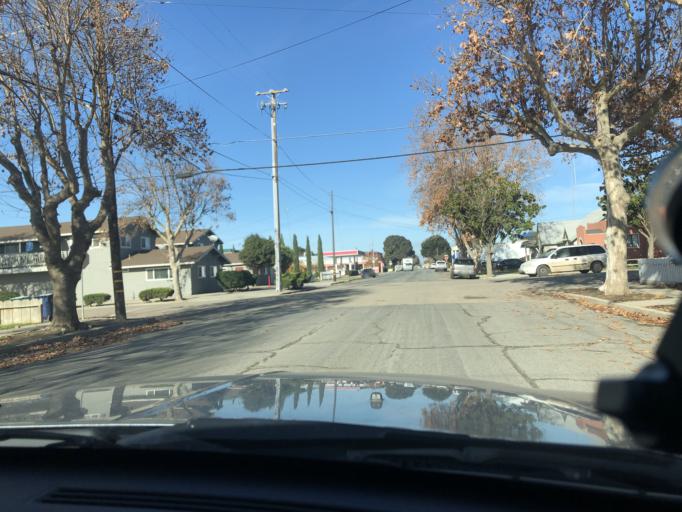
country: US
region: California
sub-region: Monterey County
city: King City
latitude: 36.2097
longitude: -121.1295
